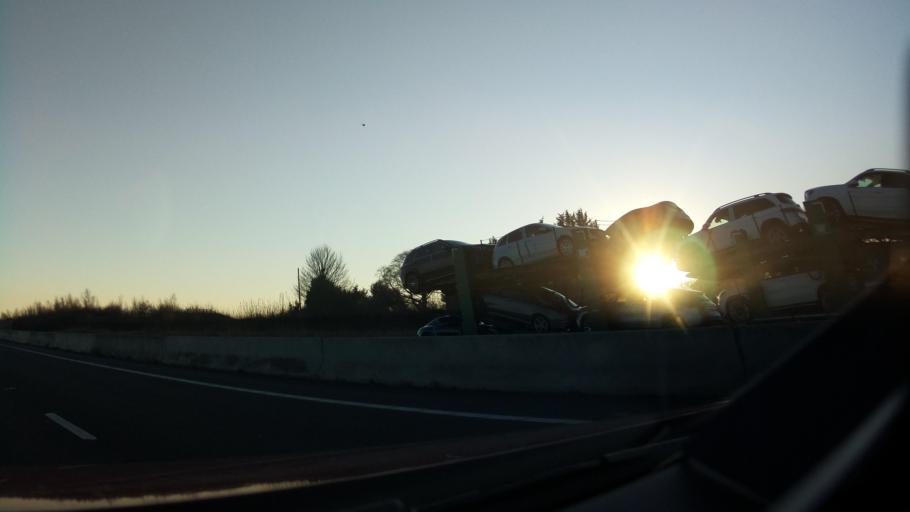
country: GB
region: England
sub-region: North Yorkshire
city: Bedale
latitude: 54.2431
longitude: -1.5010
